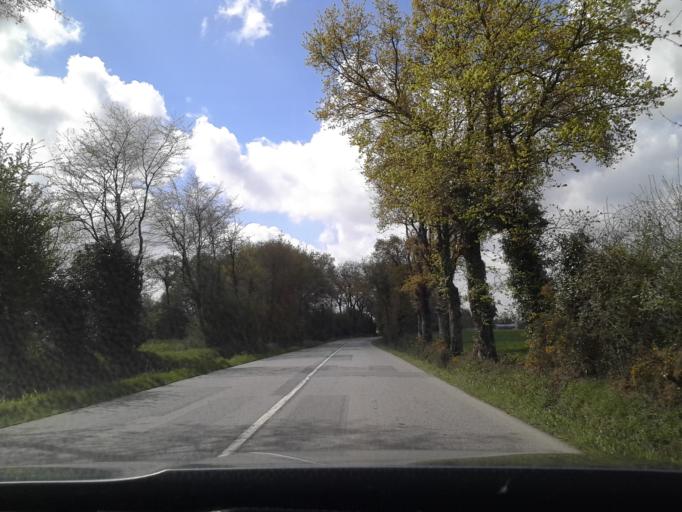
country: FR
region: Brittany
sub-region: Departement d'Ille-et-Vilaine
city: Grand-Fougeray
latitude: 47.7342
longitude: -1.7223
